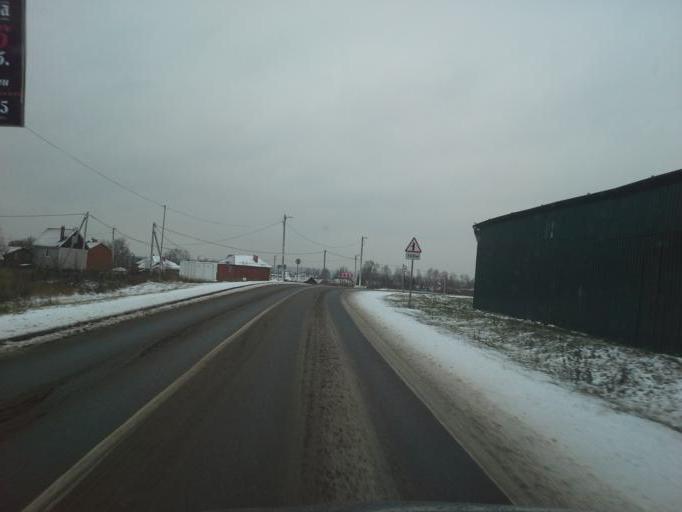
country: RU
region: Moskovskaya
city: Gorki Vtoryye
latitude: 55.7480
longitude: 37.1214
